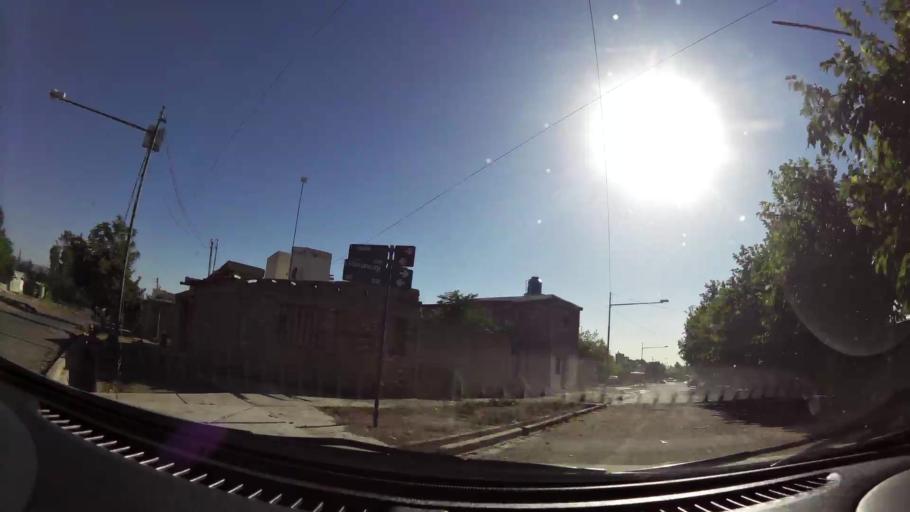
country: AR
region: Mendoza
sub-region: Departamento de Godoy Cruz
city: Godoy Cruz
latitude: -32.9267
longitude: -68.8668
